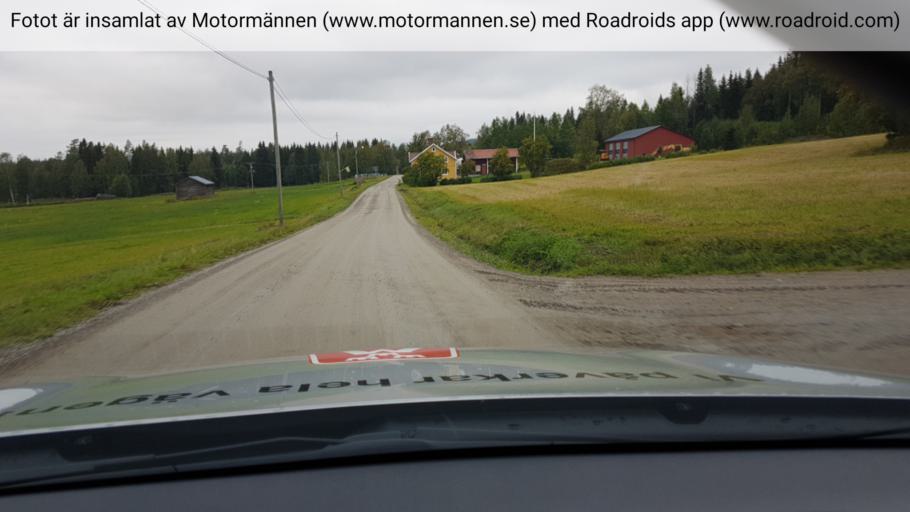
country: SE
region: Jaemtland
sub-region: Braecke Kommun
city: Braecke
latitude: 62.7741
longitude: 15.4798
